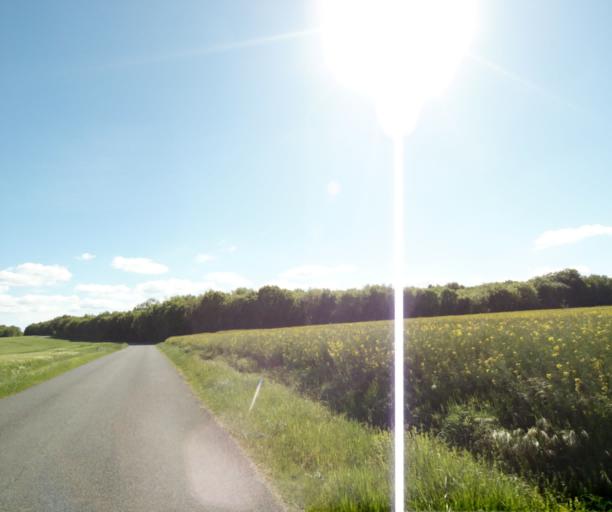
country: FR
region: Poitou-Charentes
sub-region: Departement de la Charente-Maritime
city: Bussac-sur-Charente
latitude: 45.8091
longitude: -0.6625
